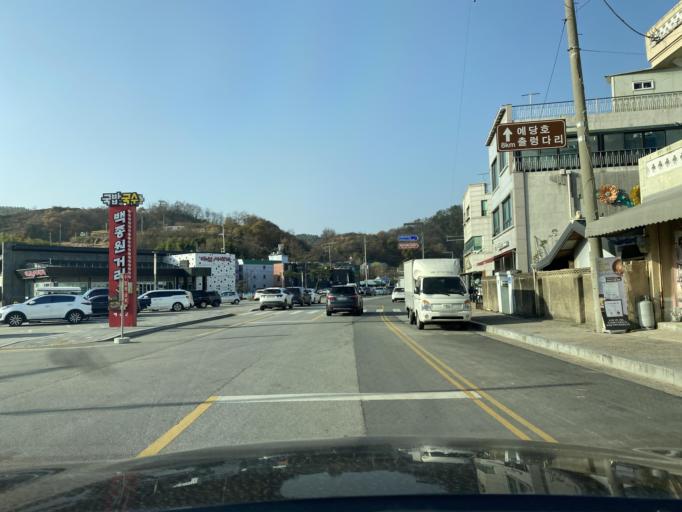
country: KR
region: Chungcheongnam-do
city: Yesan
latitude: 36.6768
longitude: 126.8485
